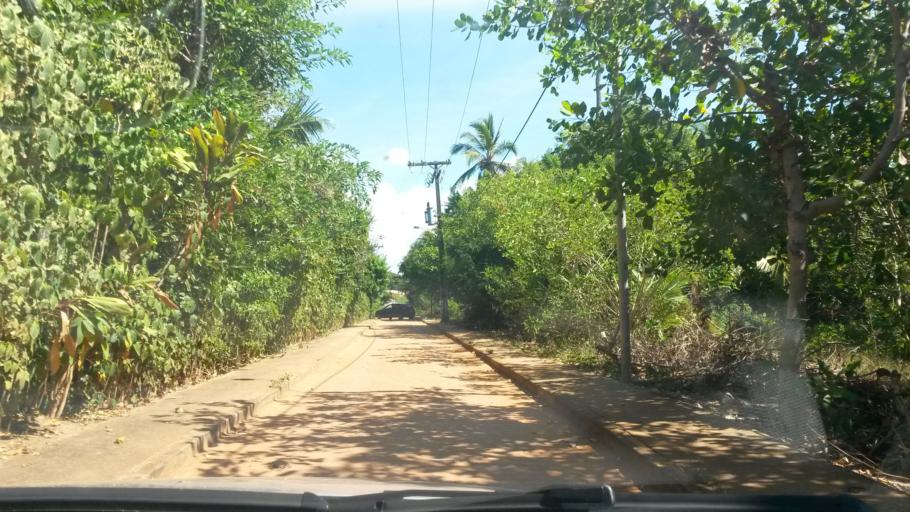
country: BR
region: Bahia
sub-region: Mata De Sao Joao
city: Mata de Sao Joao
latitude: -12.4906
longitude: -37.9576
